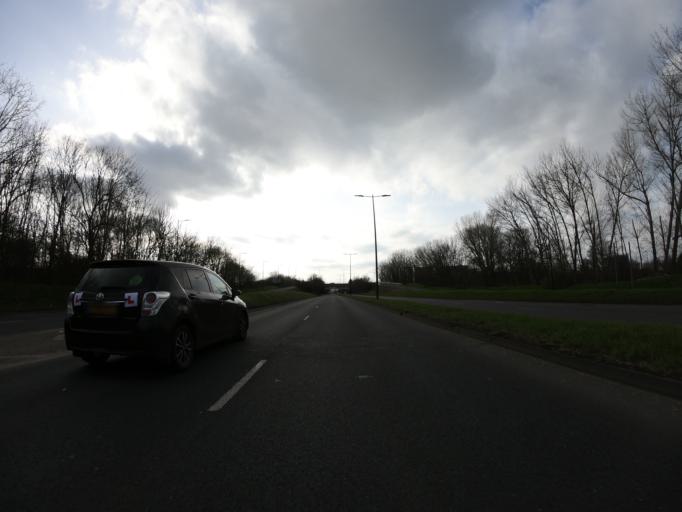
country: GB
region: England
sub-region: Greater London
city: Abbey Wood
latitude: 51.5026
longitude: 0.1247
